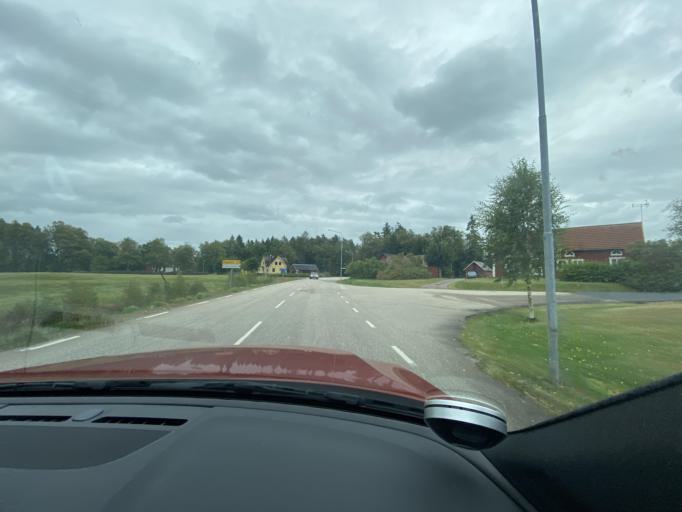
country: SE
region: Kronoberg
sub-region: Markaryds Kommun
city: Markaryd
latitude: 56.4860
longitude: 13.5305
